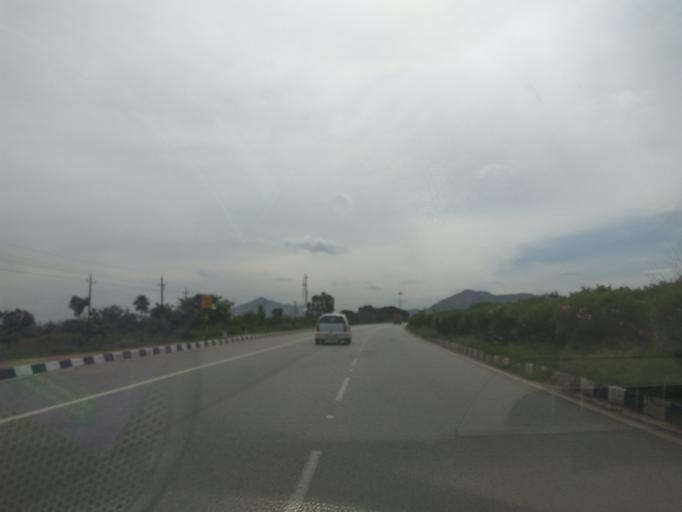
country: IN
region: Karnataka
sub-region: Kolar
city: Malur
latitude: 13.1333
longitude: 77.9779
